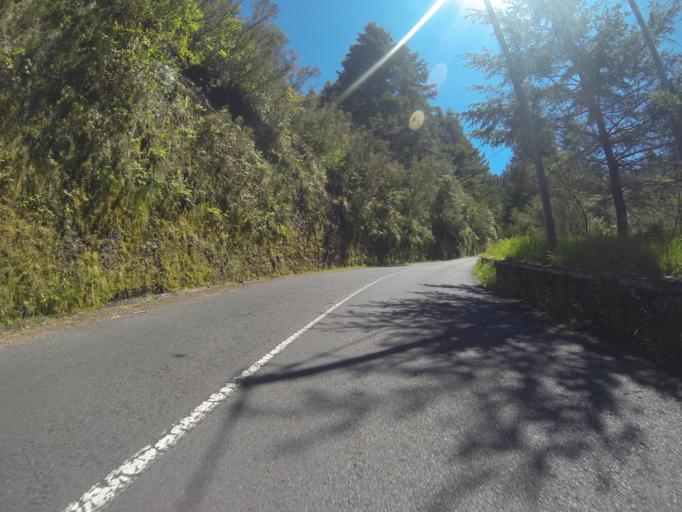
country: PT
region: Madeira
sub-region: Funchal
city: Nossa Senhora do Monte
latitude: 32.7218
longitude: -16.8895
